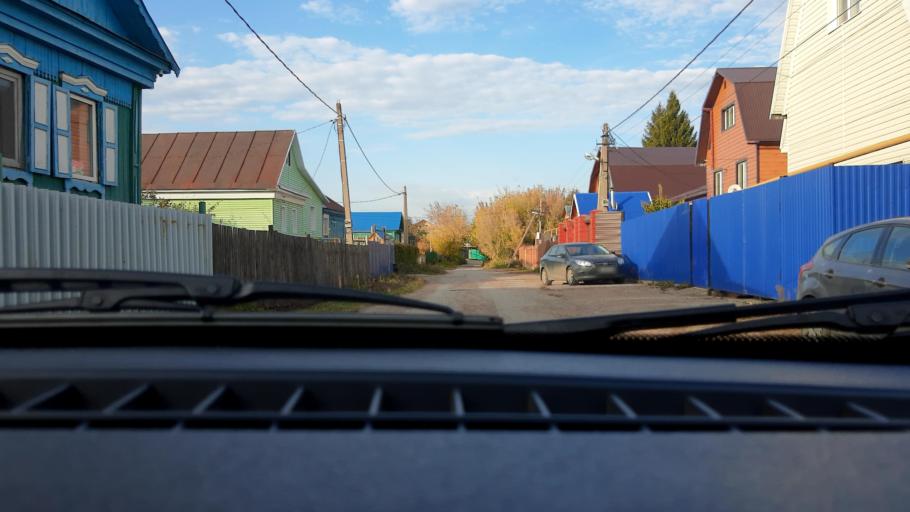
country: RU
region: Bashkortostan
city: Ufa
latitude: 54.7320
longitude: 55.8991
